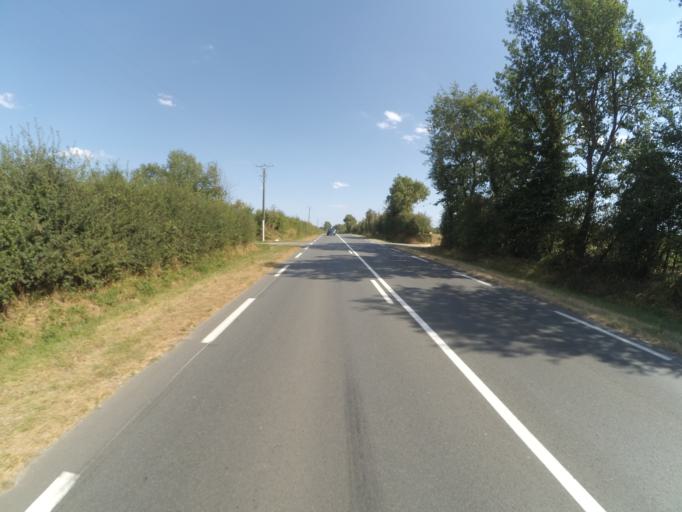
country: FR
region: Poitou-Charentes
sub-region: Departement de la Vienne
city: Savigny-Levescault
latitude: 46.5228
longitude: 0.4483
